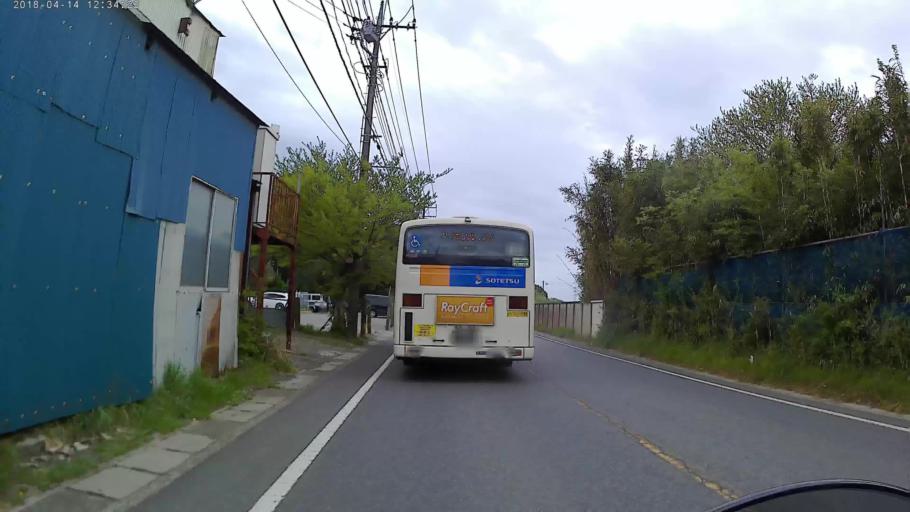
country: JP
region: Kanagawa
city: Atsugi
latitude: 35.4272
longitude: 139.4094
